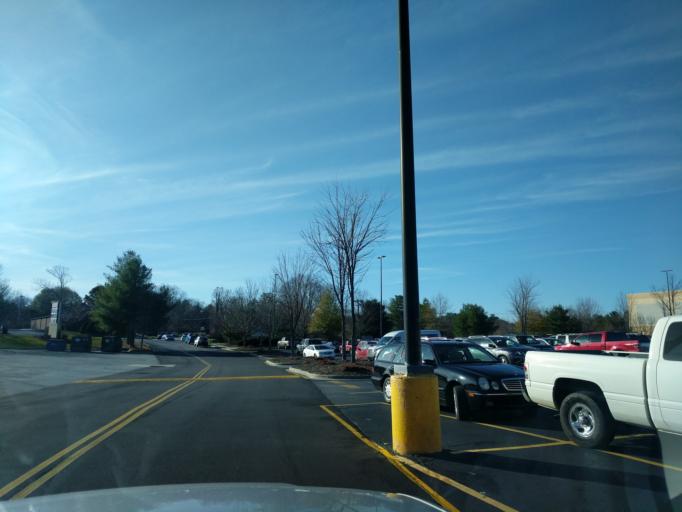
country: US
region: North Carolina
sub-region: Henderson County
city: Hendersonville
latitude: 35.3385
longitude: -82.4457
